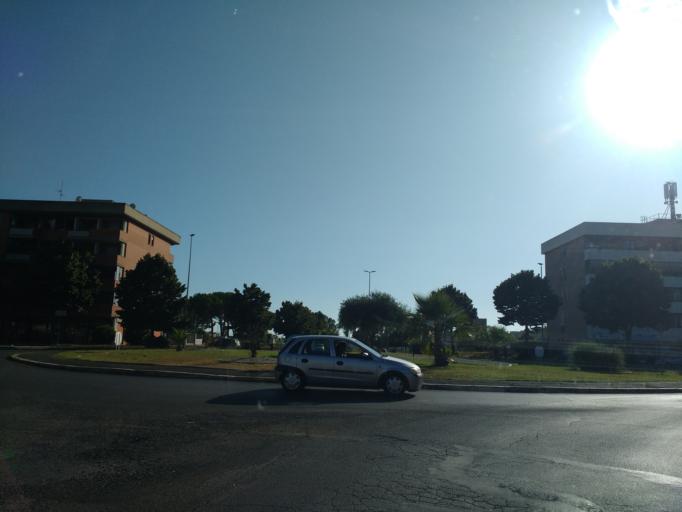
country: IT
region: Latium
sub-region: Citta metropolitana di Roma Capitale
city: Acilia-Castel Fusano-Ostia Antica
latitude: 41.7767
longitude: 12.3523
